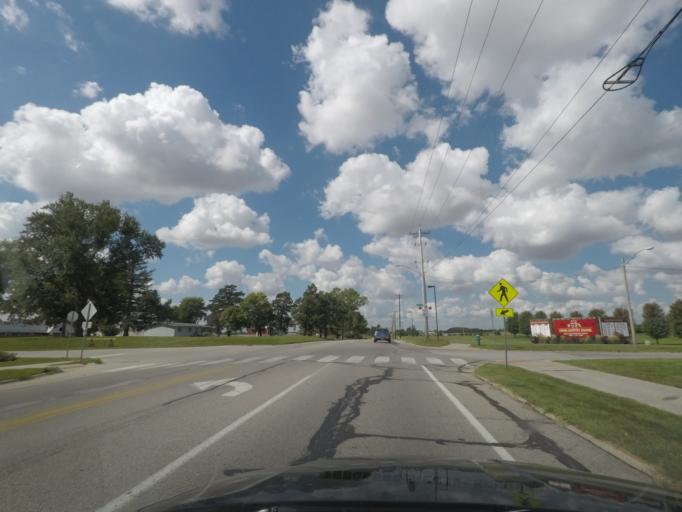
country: US
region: Iowa
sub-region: Story County
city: Ames
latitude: 42.0119
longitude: -93.6514
